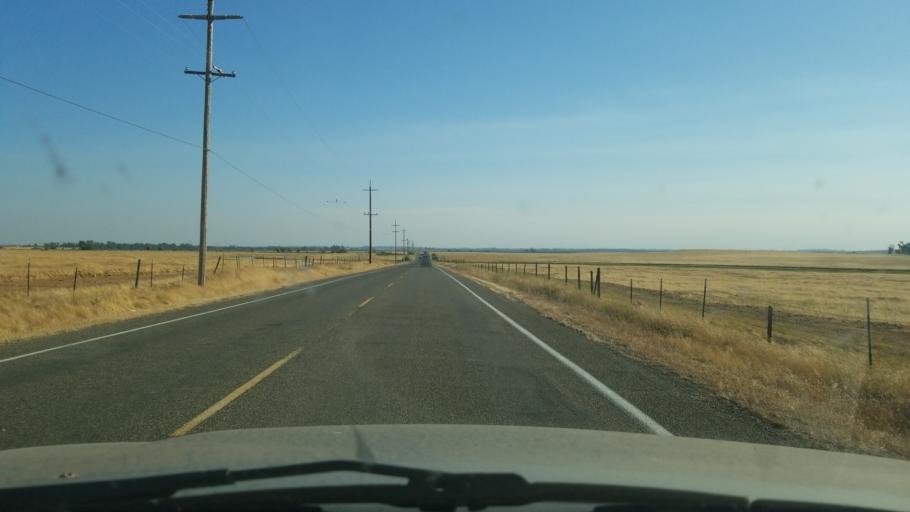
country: US
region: California
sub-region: Merced County
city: Merced
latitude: 37.4143
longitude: -120.4496
